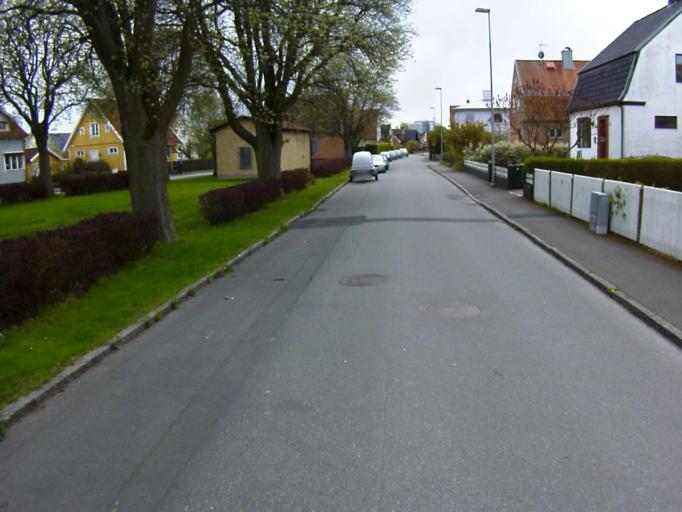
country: SE
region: Skane
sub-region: Kristianstads Kommun
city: Kristianstad
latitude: 56.0407
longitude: 14.1675
